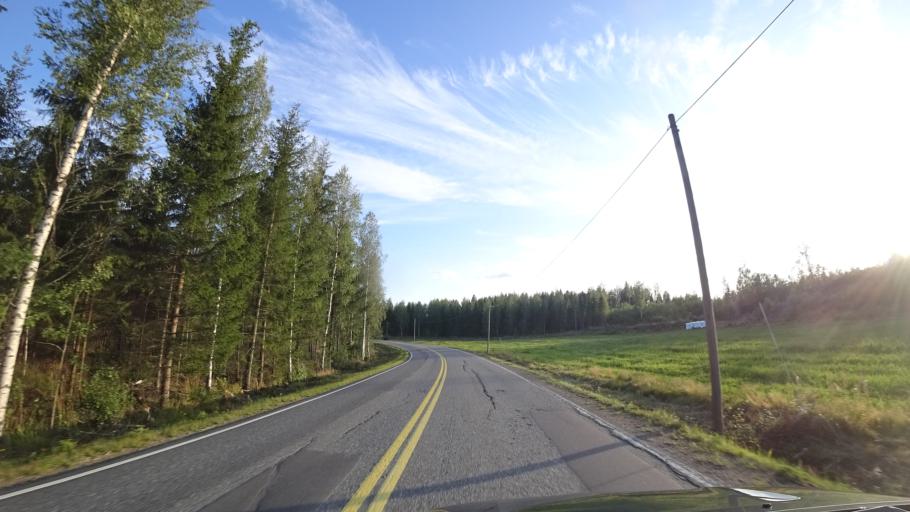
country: FI
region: Haeme
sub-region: Haemeenlinna
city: Lammi
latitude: 61.0563
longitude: 24.9645
